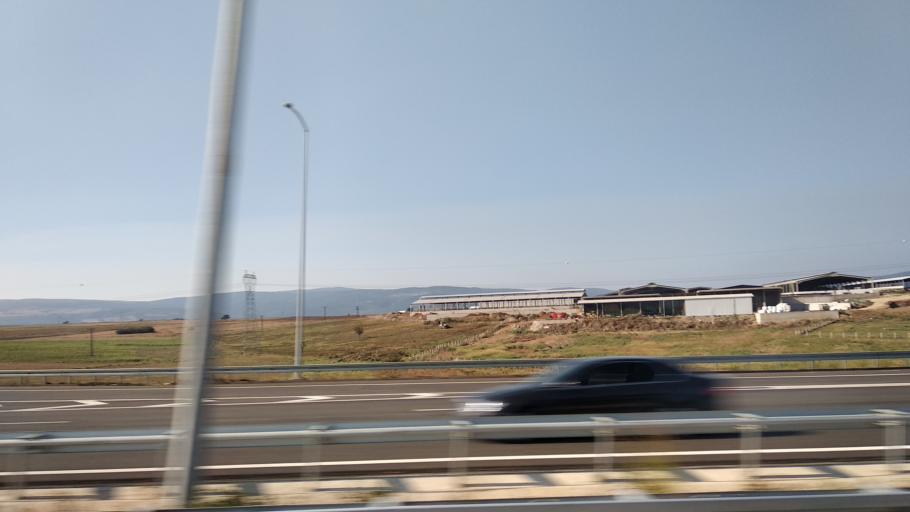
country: TR
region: Bursa
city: Karacabey
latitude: 40.2523
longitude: 28.4564
